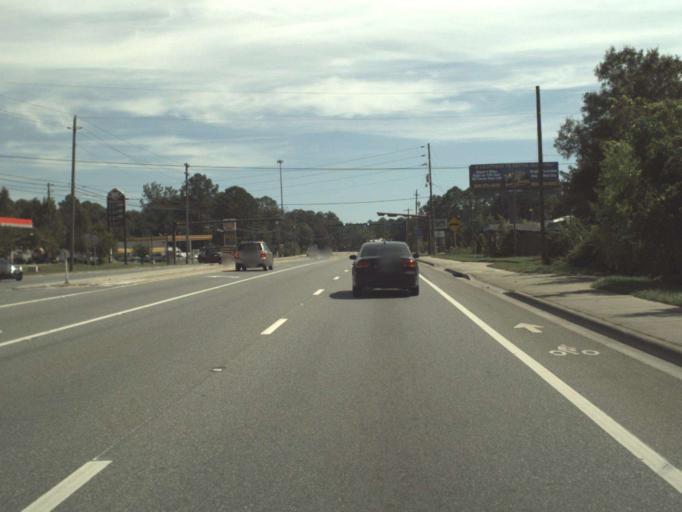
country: US
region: Florida
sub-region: Bay County
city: Lynn Haven
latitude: 30.2867
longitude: -85.6384
